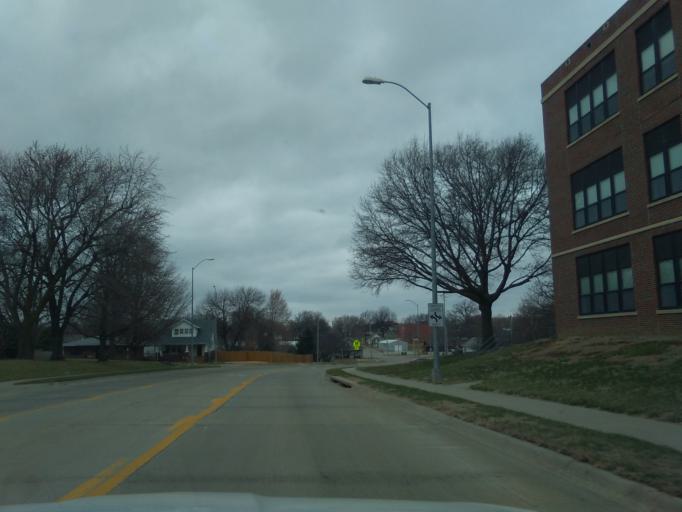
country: US
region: Nebraska
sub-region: Richardson County
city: Falls City
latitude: 40.0584
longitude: -95.5946
